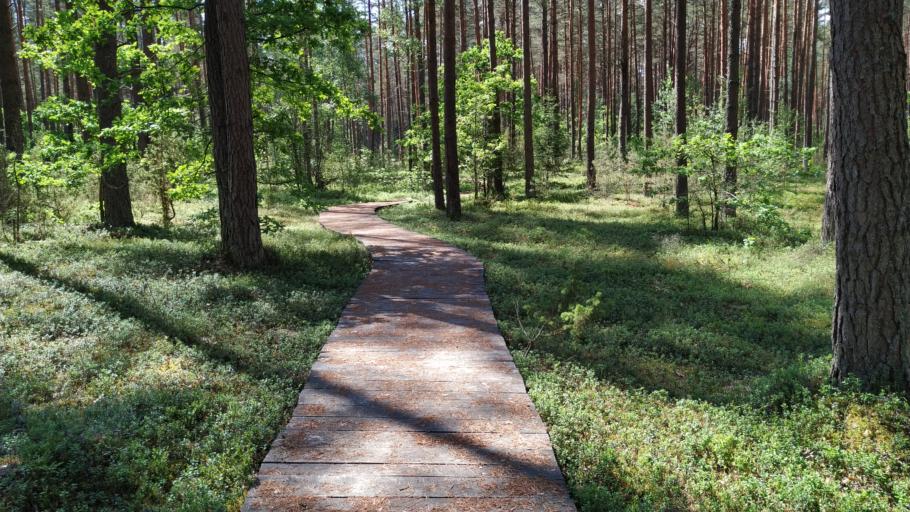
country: LT
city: Nemencine
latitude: 54.8083
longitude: 25.3968
